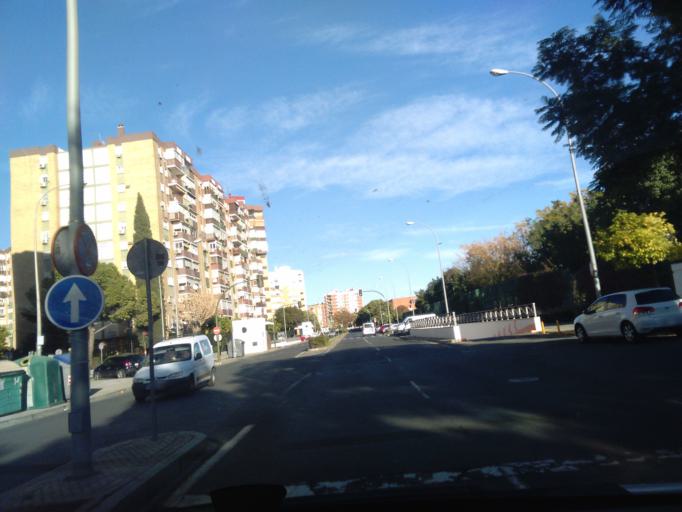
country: ES
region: Andalusia
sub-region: Provincia de Sevilla
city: Sevilla
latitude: 37.3835
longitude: -5.9471
